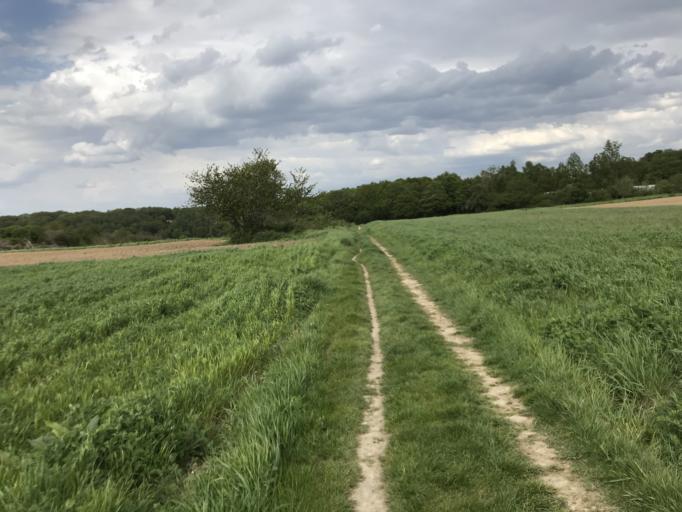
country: FR
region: Ile-de-France
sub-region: Departement de l'Essonne
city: Vauhallan
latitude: 48.7286
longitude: 2.1966
